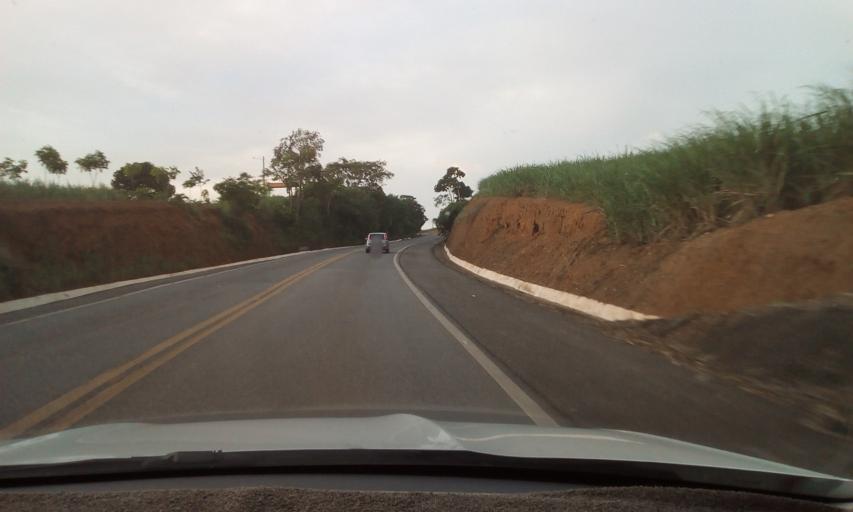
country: BR
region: Pernambuco
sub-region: Vicencia
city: Vicencia
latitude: -7.6129
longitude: -35.2397
